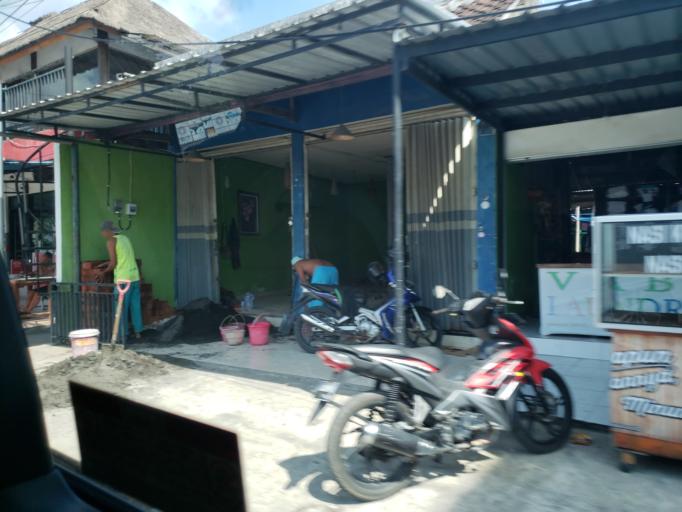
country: ID
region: Bali
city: Kangin
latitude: -8.8225
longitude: 115.1434
